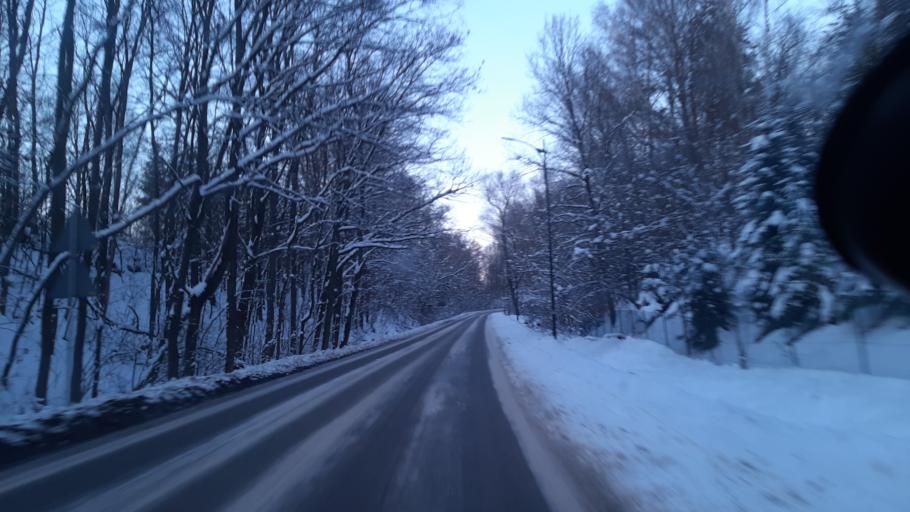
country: PL
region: Lublin Voivodeship
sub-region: Powiat lubelski
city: Lublin
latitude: 51.3150
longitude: 22.5611
